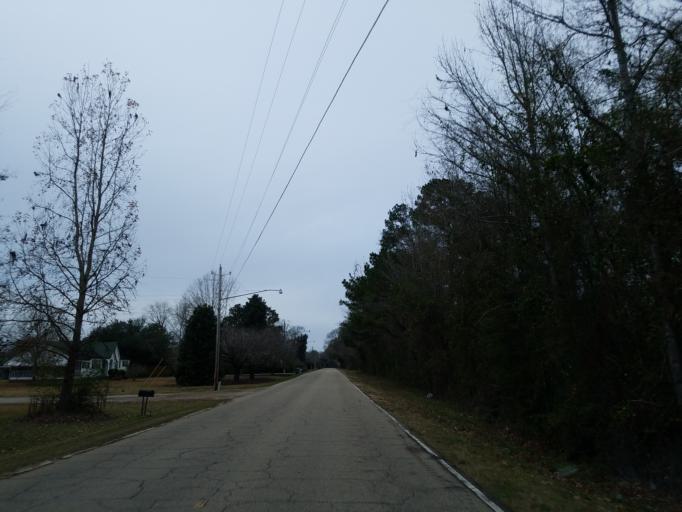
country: US
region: Mississippi
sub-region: Forrest County
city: Hattiesburg
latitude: 31.2847
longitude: -89.2567
